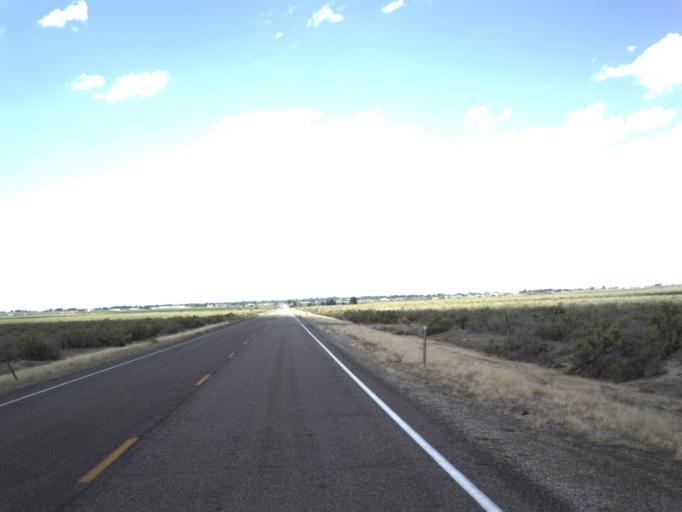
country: US
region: Utah
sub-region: Millard County
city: Delta
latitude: 39.3532
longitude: -112.5094
